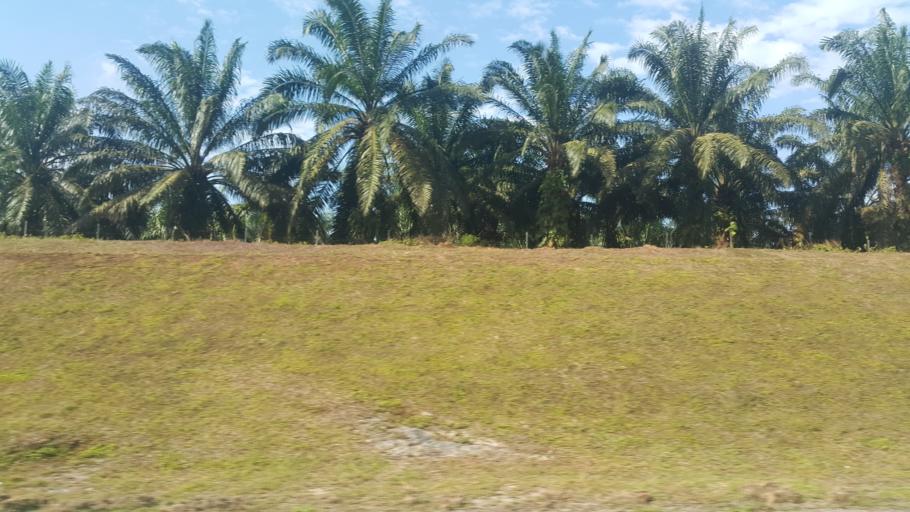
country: MY
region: Johor
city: Kelapa Sawit
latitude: 1.7247
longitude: 103.4292
